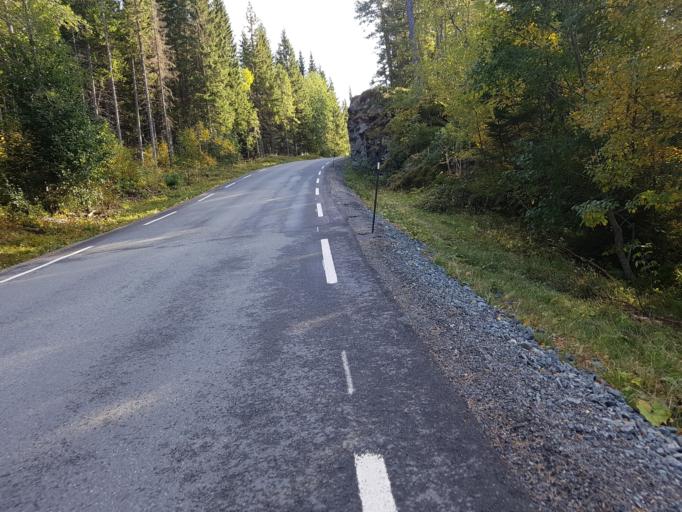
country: NO
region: Sor-Trondelag
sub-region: Malvik
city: Malvik
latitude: 63.3533
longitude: 10.6404
